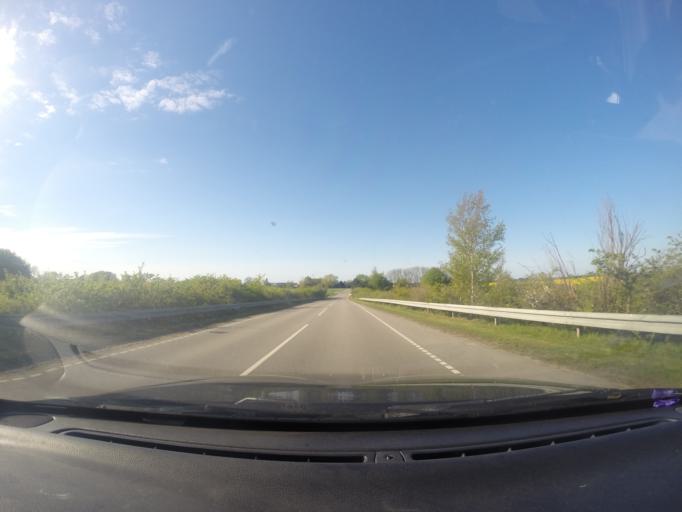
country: DK
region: Capital Region
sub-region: Hoje-Taastrup Kommune
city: Taastrup
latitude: 55.6664
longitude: 12.2539
